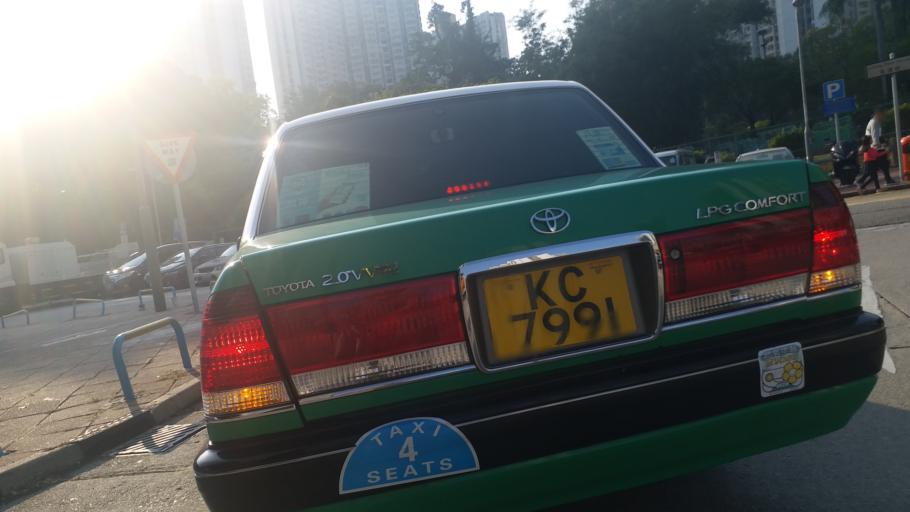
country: HK
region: Tuen Mun
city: Tuen Mun
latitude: 22.4061
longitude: 113.9688
